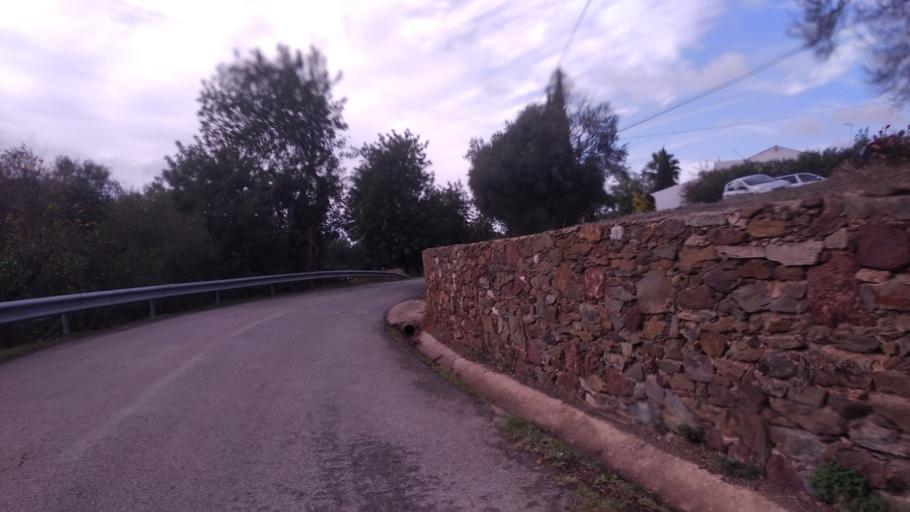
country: PT
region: Faro
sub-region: Sao Bras de Alportel
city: Sao Bras de Alportel
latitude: 37.1748
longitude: -7.8982
